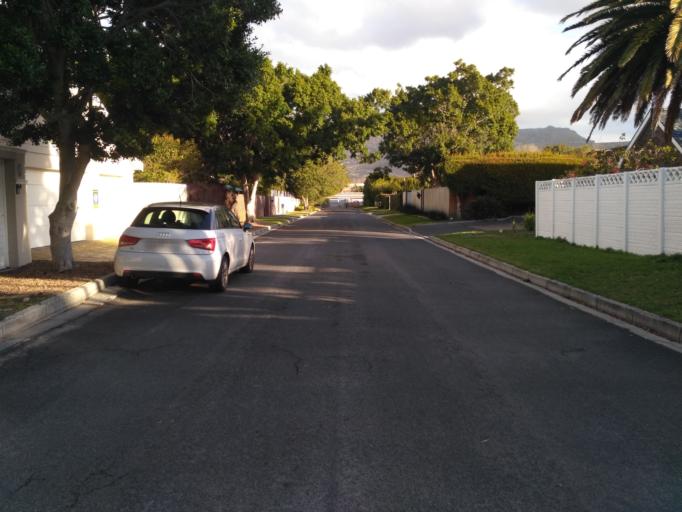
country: ZA
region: Western Cape
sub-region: City of Cape Town
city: Bergvliet
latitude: -34.0615
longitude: 18.4439
